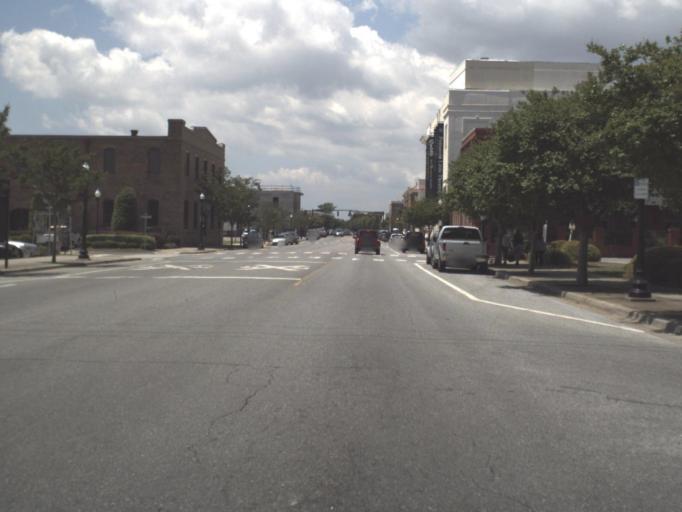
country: US
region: Florida
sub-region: Escambia County
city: Pensacola
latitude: 30.4081
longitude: -87.2116
